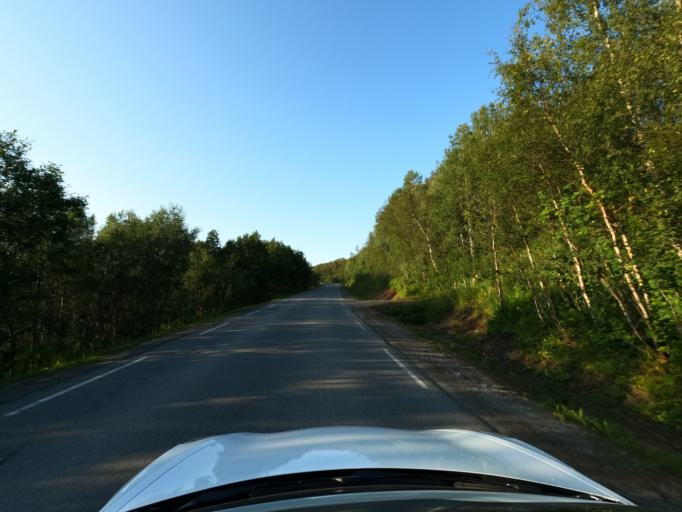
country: NO
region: Troms
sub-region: Skanland
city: Evenskjer
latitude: 68.4867
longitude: 16.7127
